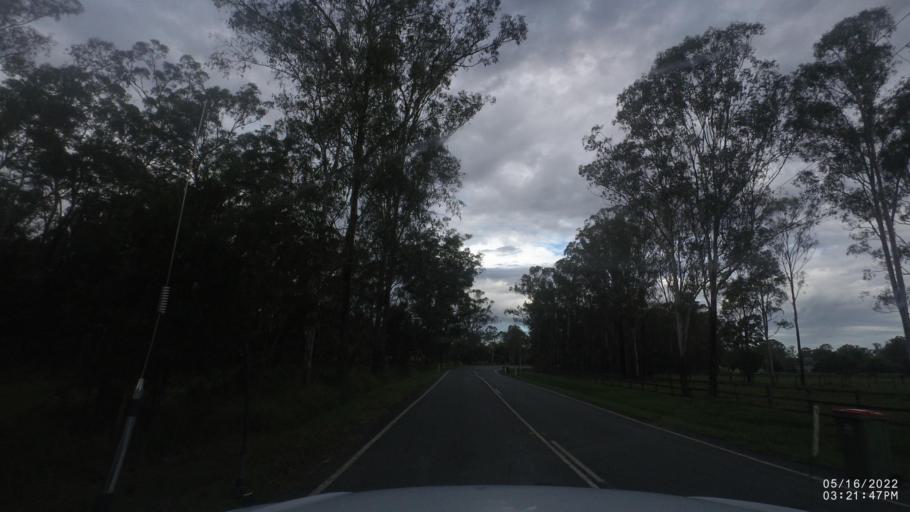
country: AU
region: Queensland
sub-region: Logan
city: Chambers Flat
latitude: -27.7460
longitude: 153.0725
